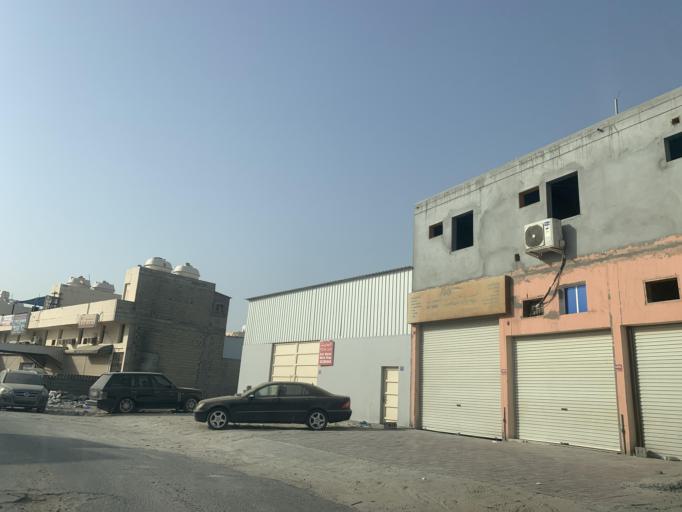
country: BH
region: Central Governorate
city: Madinat Hamad
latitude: 26.1448
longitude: 50.4851
